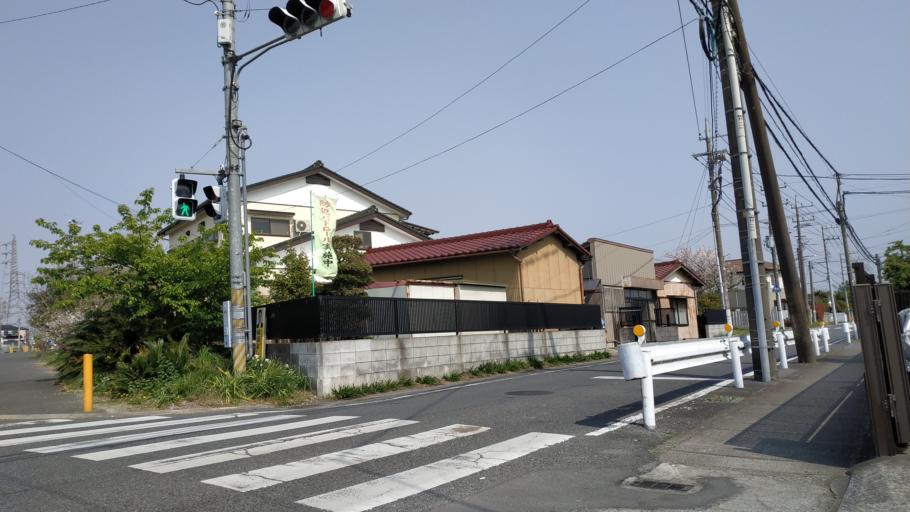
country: JP
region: Chiba
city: Ichihara
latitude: 35.5071
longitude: 140.0907
